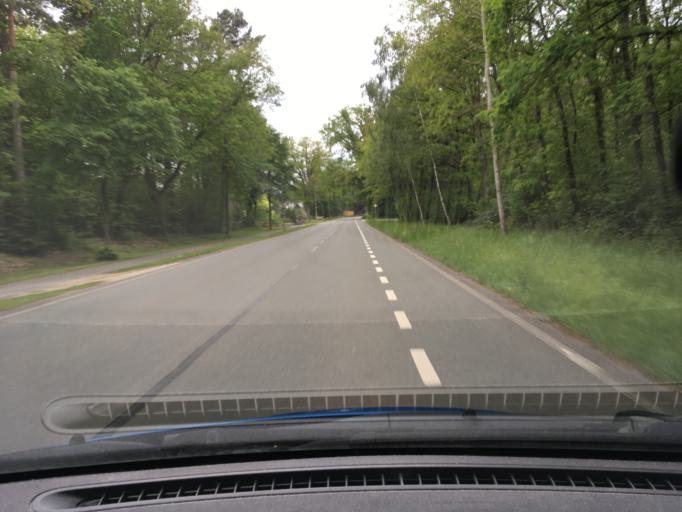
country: DE
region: Lower Saxony
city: Bispingen
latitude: 53.0946
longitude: 10.0315
